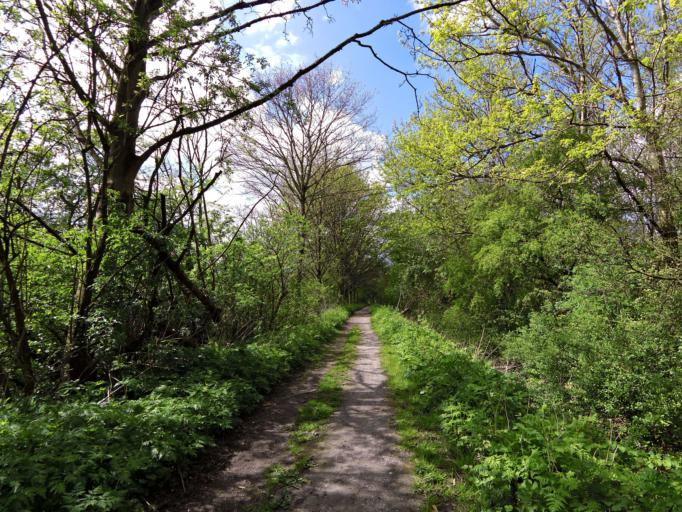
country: NL
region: South Holland
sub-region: Gemeente Albrandswaard
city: Rhoon
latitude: 51.8382
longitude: 4.4466
